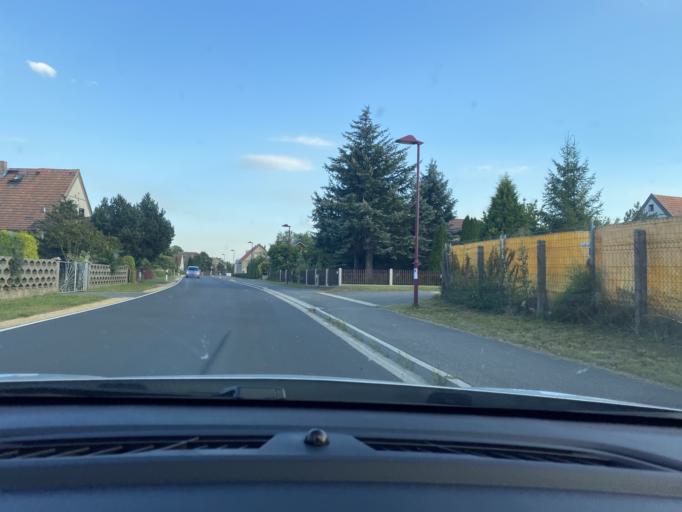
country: DE
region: Saxony
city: Kodersdorf
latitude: 51.2659
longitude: 14.8843
